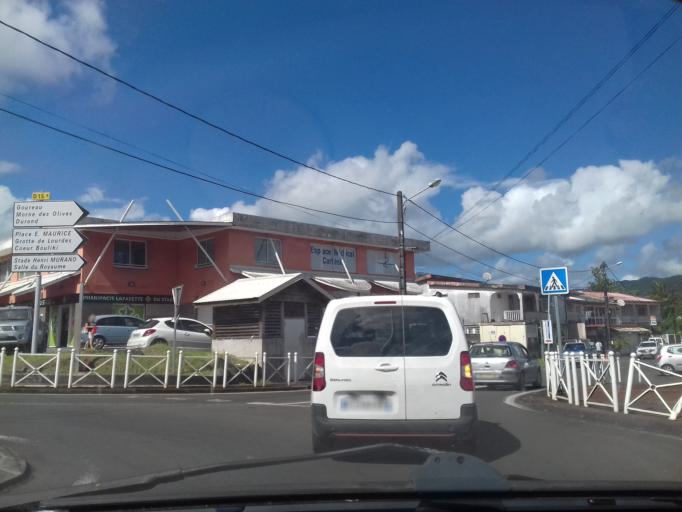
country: MQ
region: Martinique
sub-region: Martinique
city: Saint-Joseph
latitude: 14.6727
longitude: -61.0354
